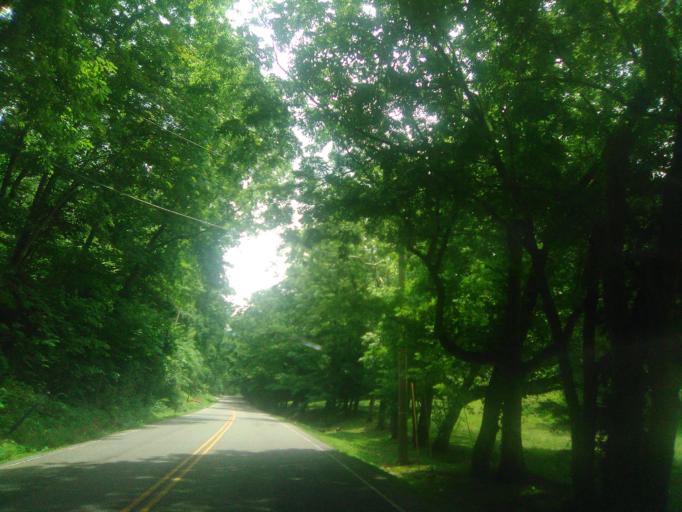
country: US
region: Tennessee
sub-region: Davidson County
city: Forest Hills
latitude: 36.0689
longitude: -86.8721
